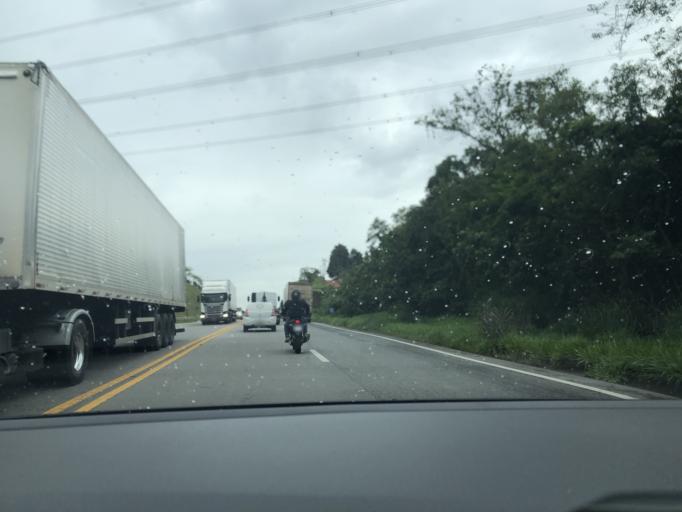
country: BR
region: Sao Paulo
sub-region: Jarinu
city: Jarinu
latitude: -23.1348
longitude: -46.7393
